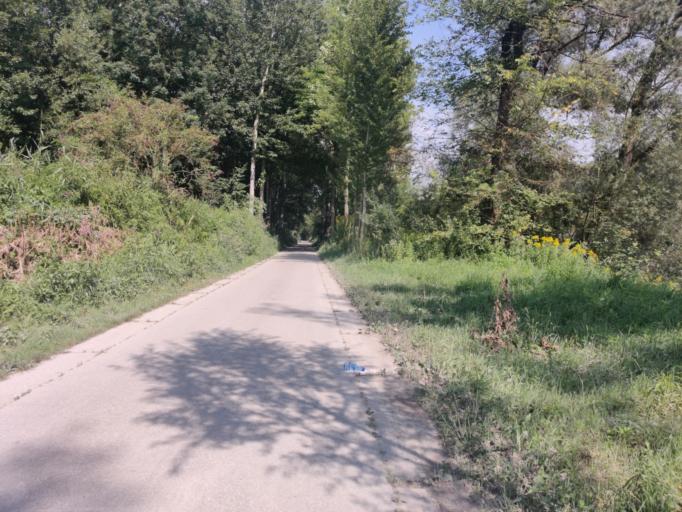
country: AT
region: Lower Austria
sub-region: Politischer Bezirk Amstetten
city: Zeillern
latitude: 48.1860
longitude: 14.7936
